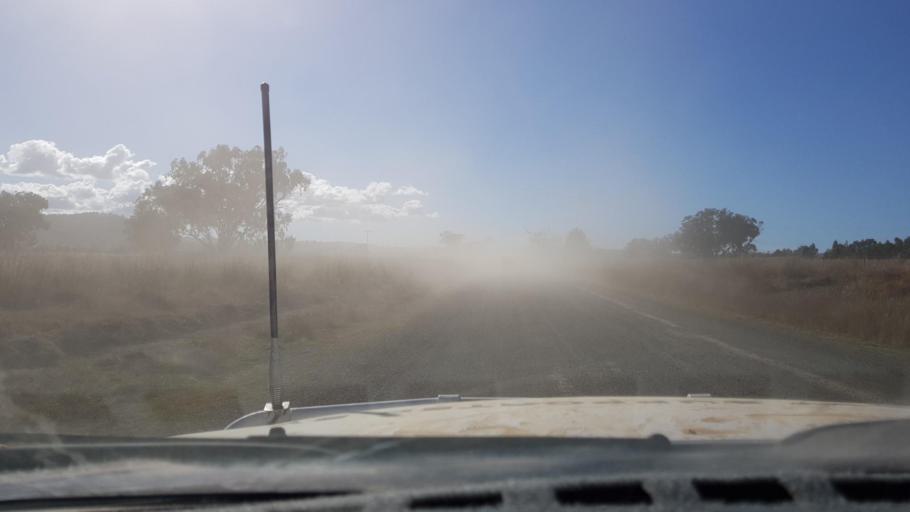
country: AU
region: New South Wales
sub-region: Narrabri
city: Blair Athol
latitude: -30.6726
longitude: 150.4508
